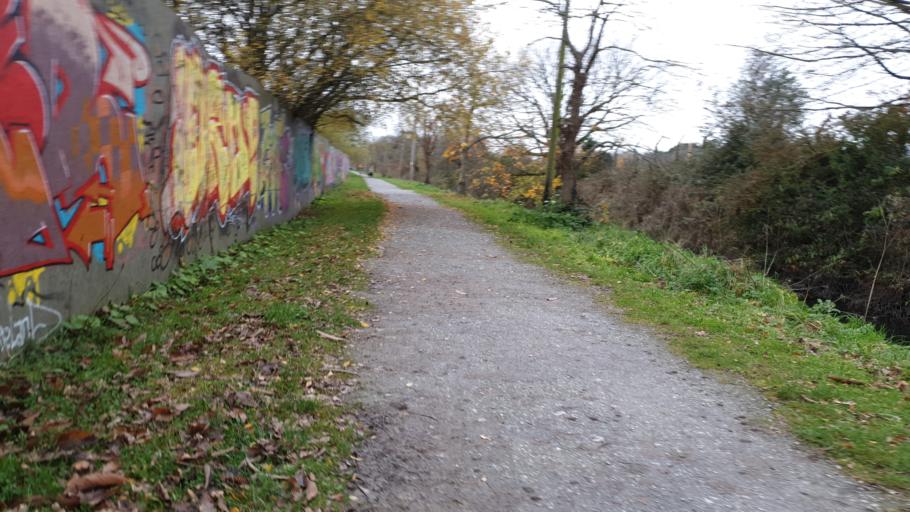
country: IE
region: Munster
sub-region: County Cork
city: Cork
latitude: 51.8996
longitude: -8.4383
